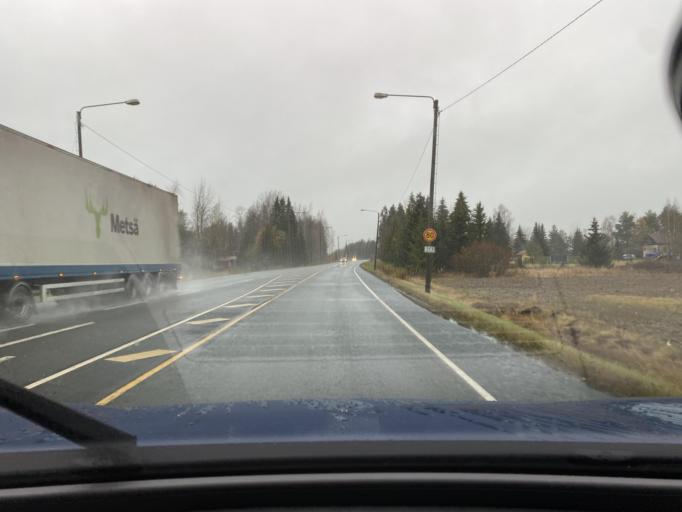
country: FI
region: Varsinais-Suomi
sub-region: Loimaa
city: Loimaa
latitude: 60.8701
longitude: 23.0029
